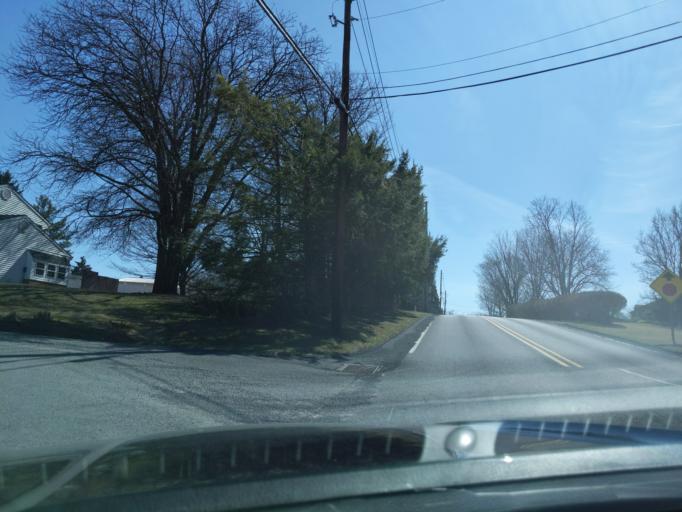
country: US
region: Pennsylvania
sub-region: Blair County
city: Duncansville
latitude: 40.4173
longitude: -78.4200
